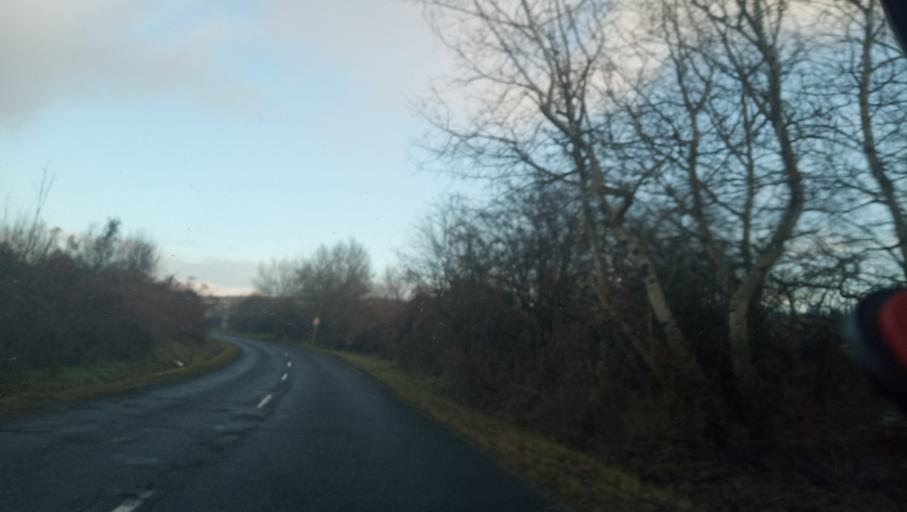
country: HU
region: Pest
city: Csobanka
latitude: 47.6314
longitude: 18.9548
